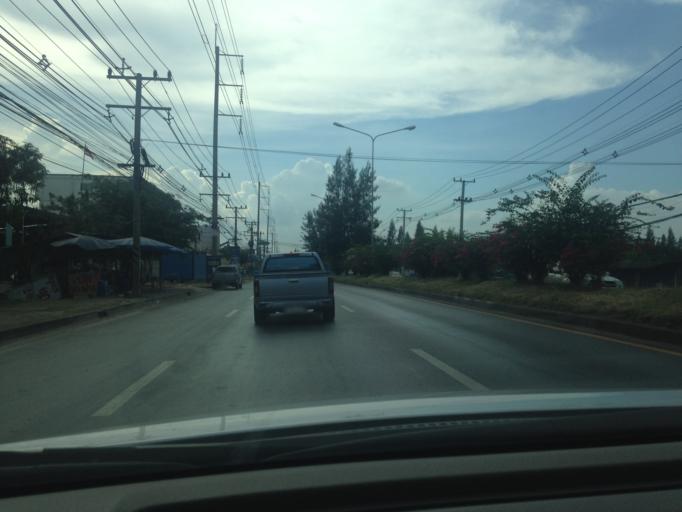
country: TH
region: Pathum Thani
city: Khlong Luang
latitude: 14.0663
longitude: 100.6771
